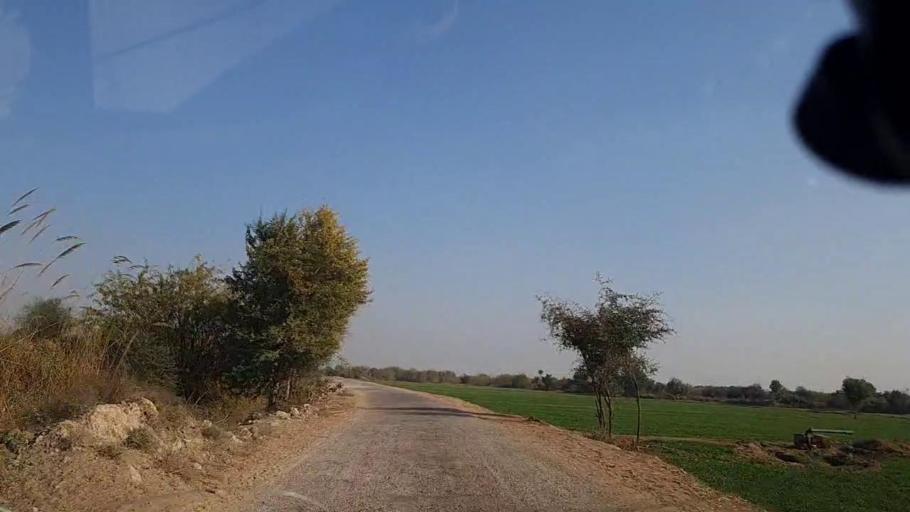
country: PK
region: Sindh
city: Khanpur
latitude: 27.6829
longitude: 69.5323
